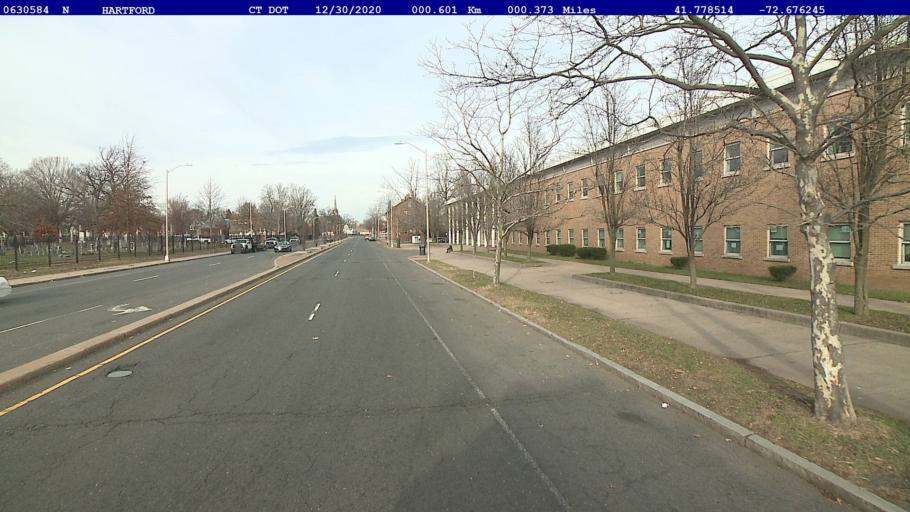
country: US
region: Connecticut
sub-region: Hartford County
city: Hartford
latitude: 41.7785
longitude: -72.6763
